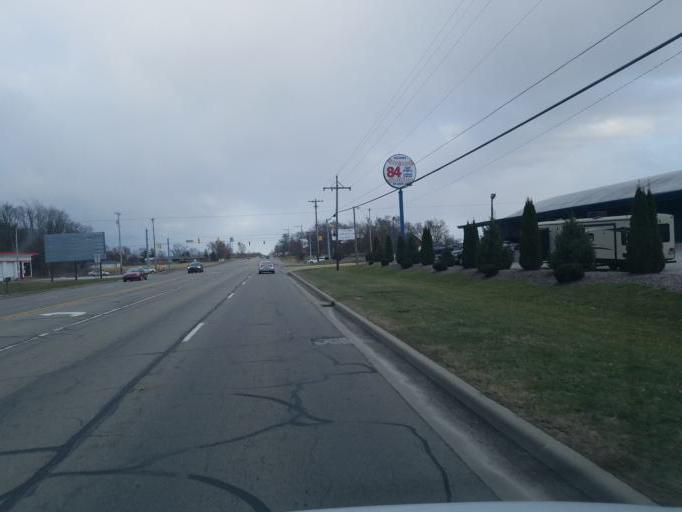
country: US
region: Indiana
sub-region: Hancock County
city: Greenfield
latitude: 39.7818
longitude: -85.8412
